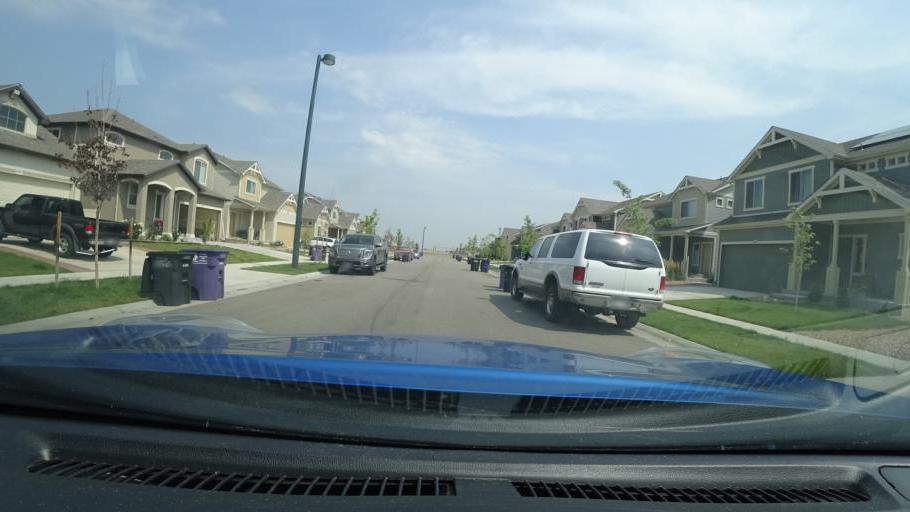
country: US
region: Colorado
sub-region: Adams County
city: Aurora
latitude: 39.7777
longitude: -104.7819
